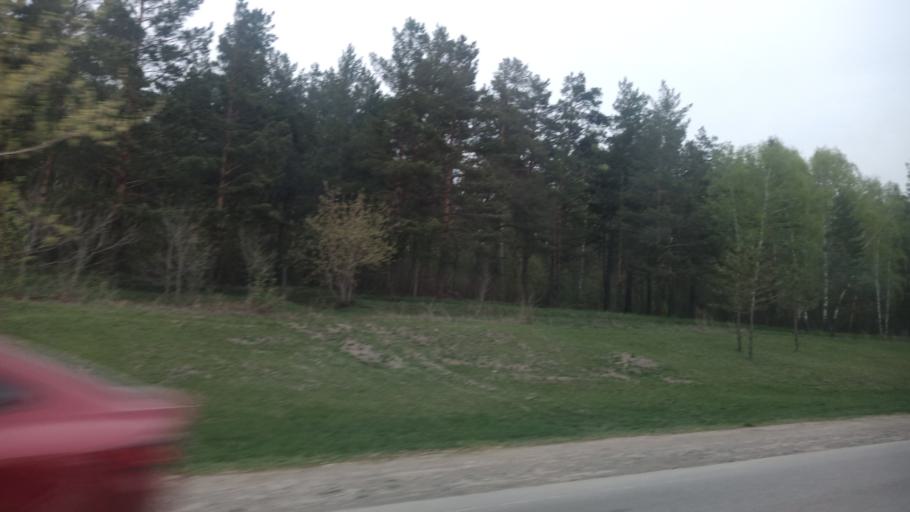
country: RU
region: Altai Krai
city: Yuzhnyy
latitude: 53.2628
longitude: 83.7041
